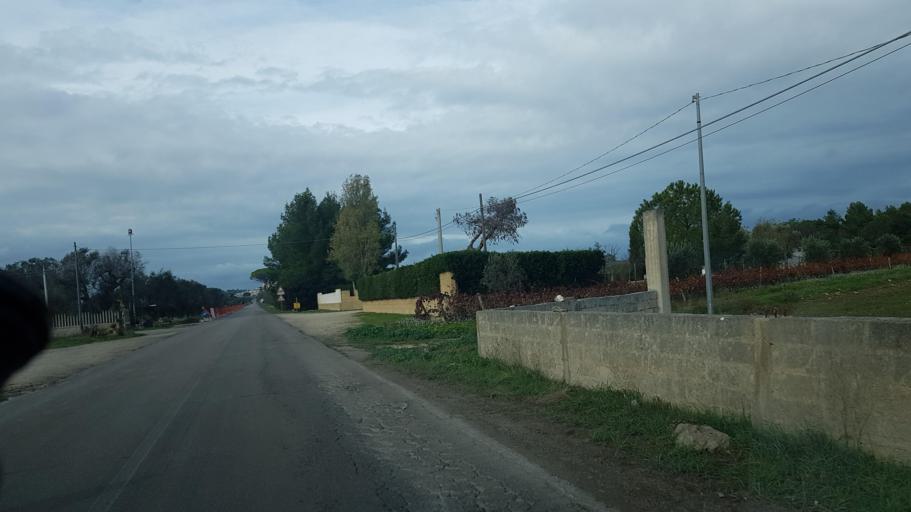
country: IT
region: Apulia
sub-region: Provincia di Brindisi
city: Oria
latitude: 40.4869
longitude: 17.6709
